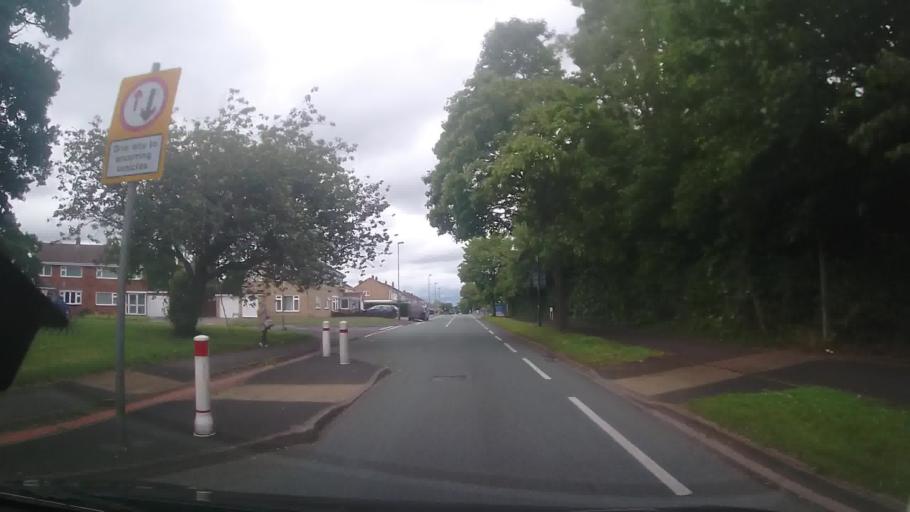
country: GB
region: England
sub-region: Shropshire
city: Shrewsbury
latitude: 52.7311
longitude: -2.7405
